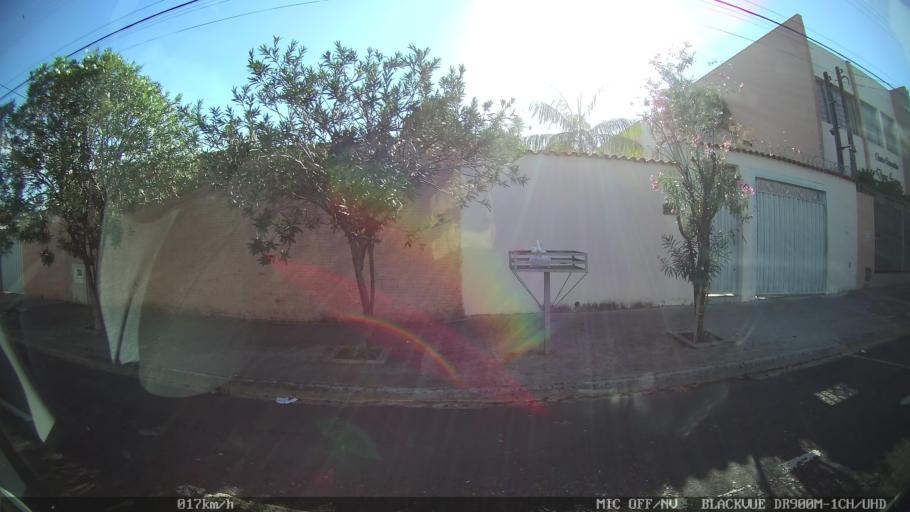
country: BR
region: Sao Paulo
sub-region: Franca
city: Franca
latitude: -20.5020
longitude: -47.4174
